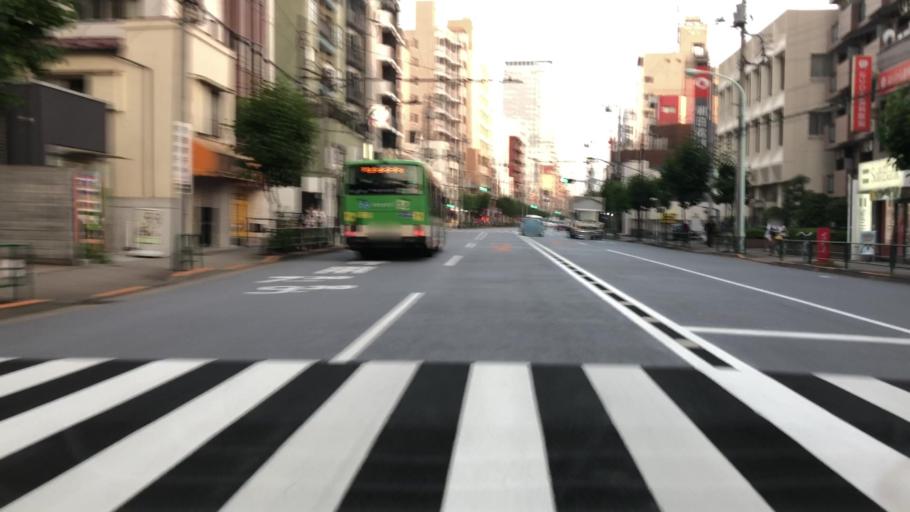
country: JP
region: Tokyo
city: Urayasu
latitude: 35.7075
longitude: 139.8140
